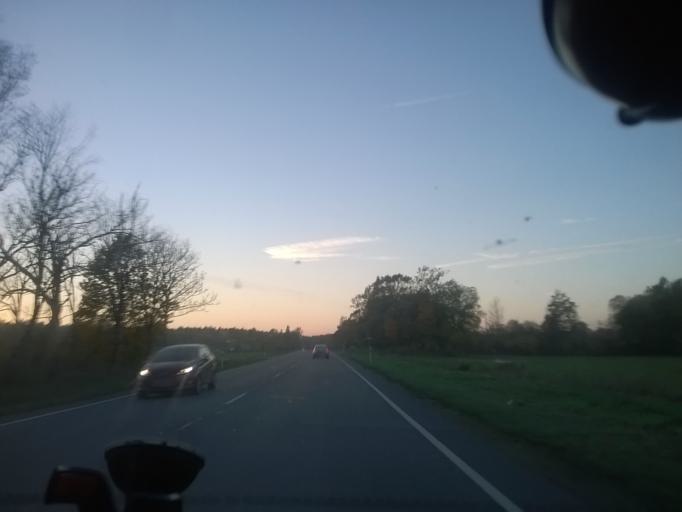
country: EE
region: Laeaene
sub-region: Ridala Parish
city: Uuemoisa
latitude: 58.9596
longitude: 23.7110
